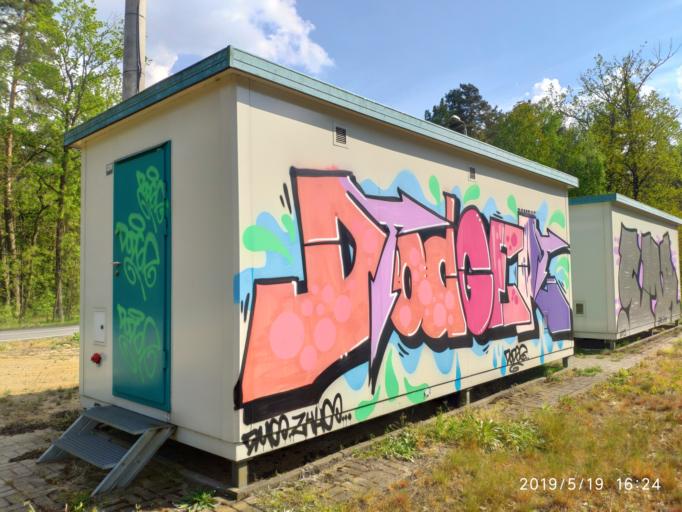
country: PL
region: Lubusz
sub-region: Powiat zielonogorski
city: Czerwiensk
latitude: 52.0131
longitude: 15.4390
